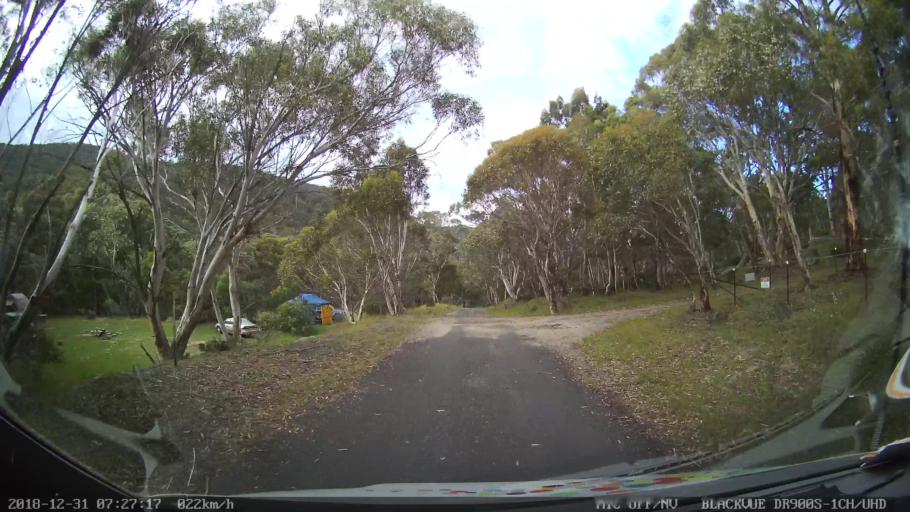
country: AU
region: New South Wales
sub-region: Snowy River
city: Jindabyne
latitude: -36.3208
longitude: 148.4802
